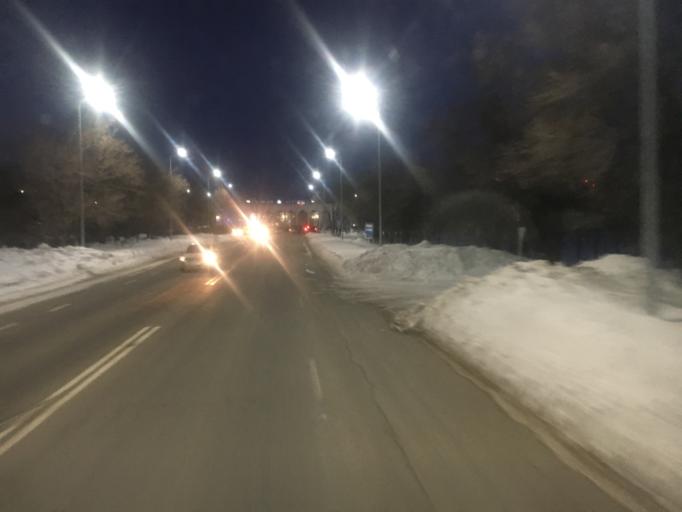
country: KZ
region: Batys Qazaqstan
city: Oral
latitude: 51.1553
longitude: 51.5363
